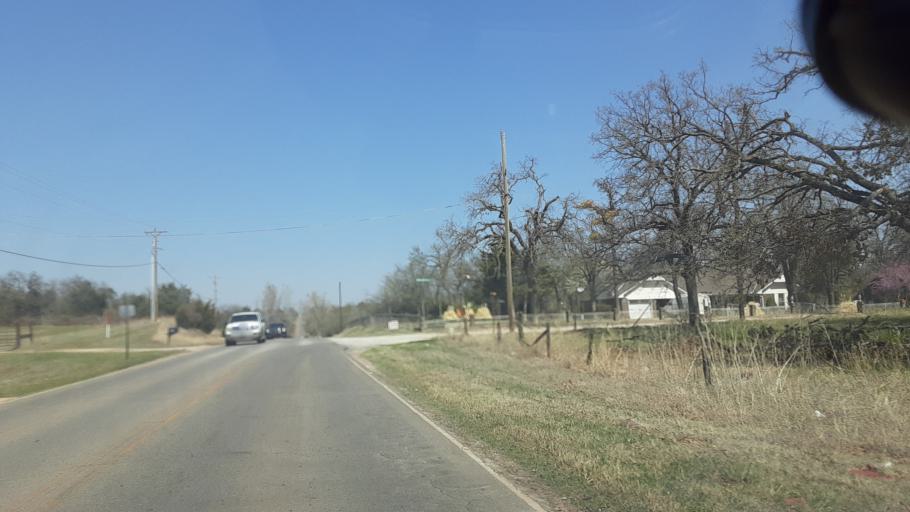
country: US
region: Oklahoma
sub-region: Oklahoma County
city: Edmond
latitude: 35.7513
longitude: -97.4783
